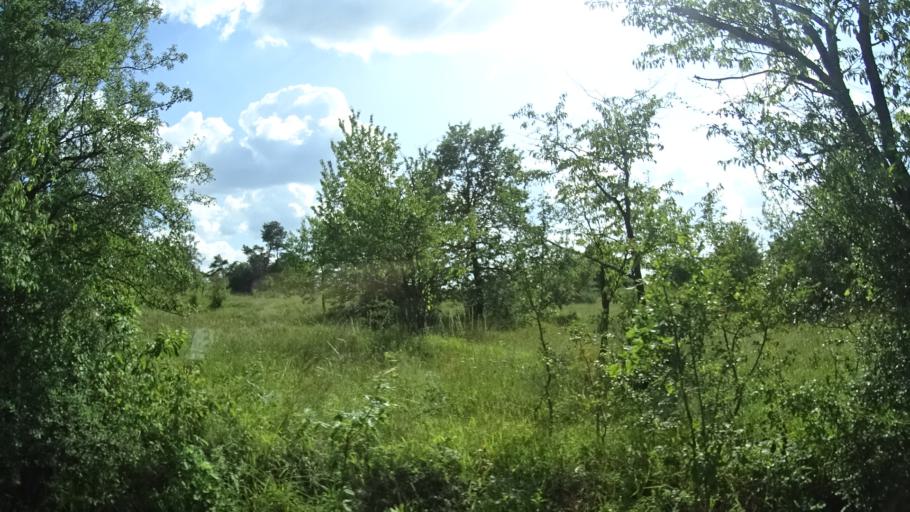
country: DE
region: Bavaria
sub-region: Regierungsbezirk Unterfranken
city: Trappstadt
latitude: 50.2847
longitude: 10.5882
